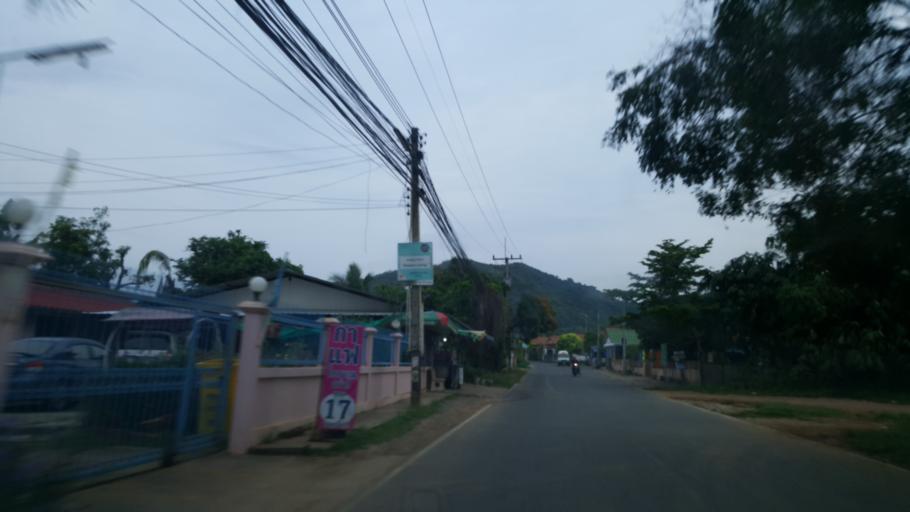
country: TH
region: Chon Buri
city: Sattahip
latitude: 12.6912
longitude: 100.9077
